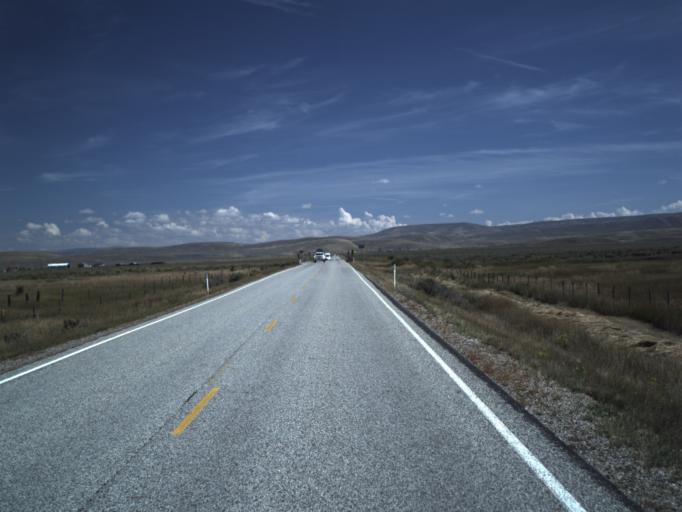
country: US
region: Utah
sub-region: Rich County
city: Randolph
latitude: 41.7768
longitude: -111.0759
